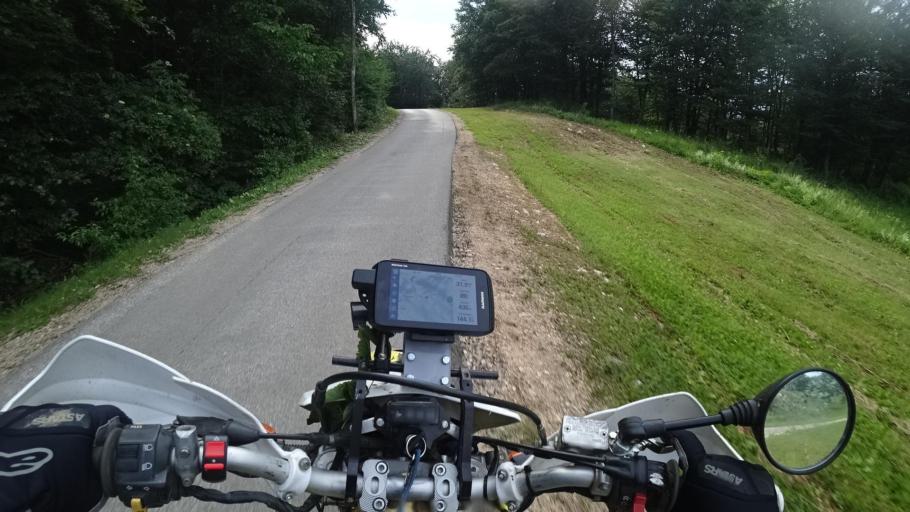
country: HR
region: Licko-Senjska
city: Jezerce
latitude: 44.9140
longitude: 15.6277
